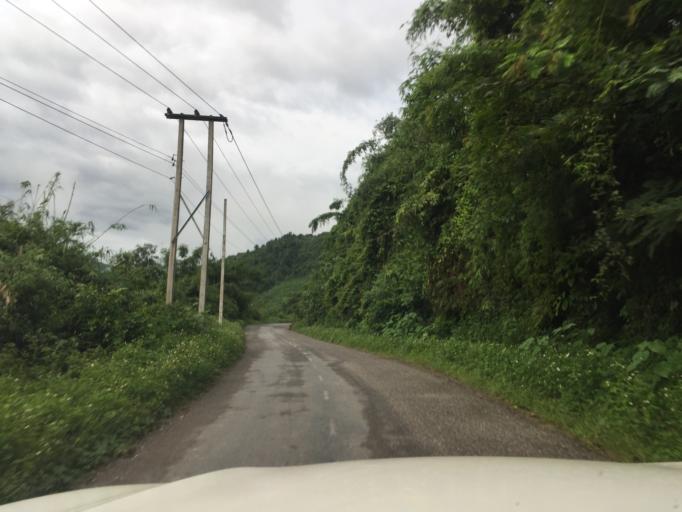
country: LA
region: Oudomxai
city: Muang La
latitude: 21.0691
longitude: 102.2413
